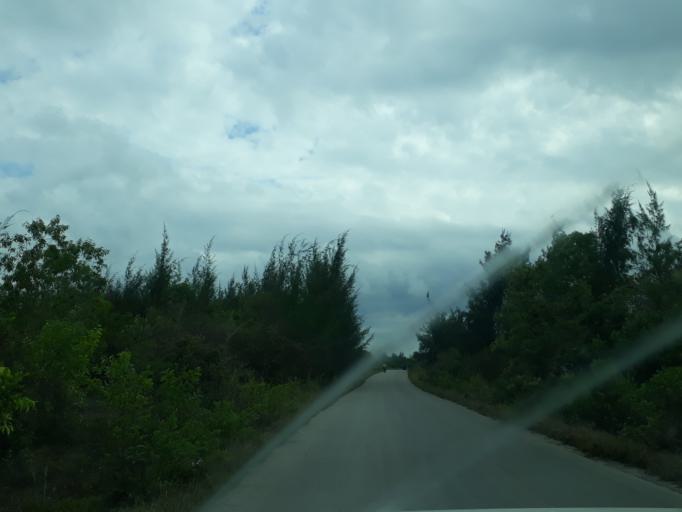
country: TZ
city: Kiwengwa
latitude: -6.0826
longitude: 39.4255
